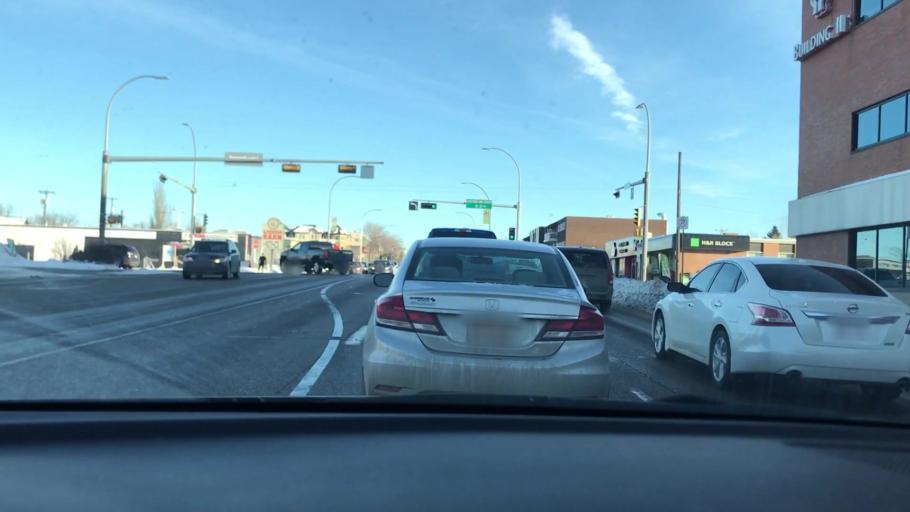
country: CA
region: Alberta
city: Edmonton
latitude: 53.5180
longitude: -113.4683
